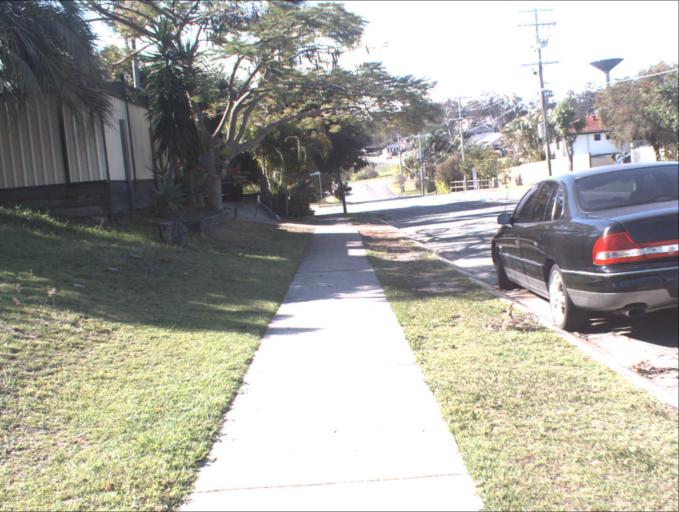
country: AU
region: Queensland
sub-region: Logan
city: Park Ridge South
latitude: -27.6816
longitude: 153.0271
